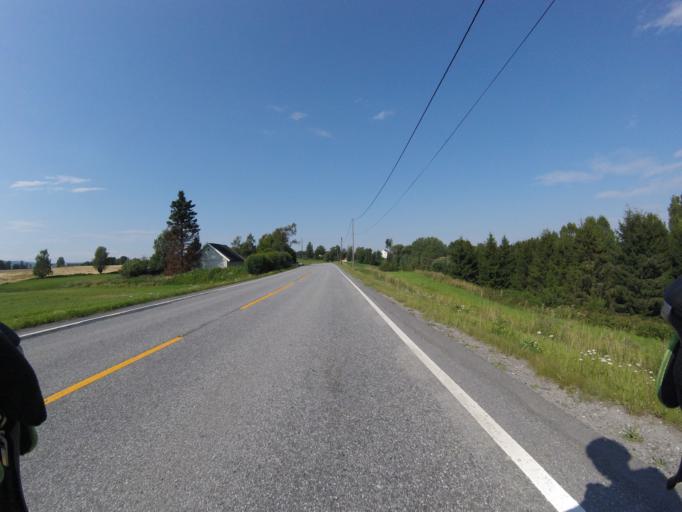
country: NO
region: Akershus
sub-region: Ullensaker
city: Klofta
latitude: 60.0518
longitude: 11.1186
